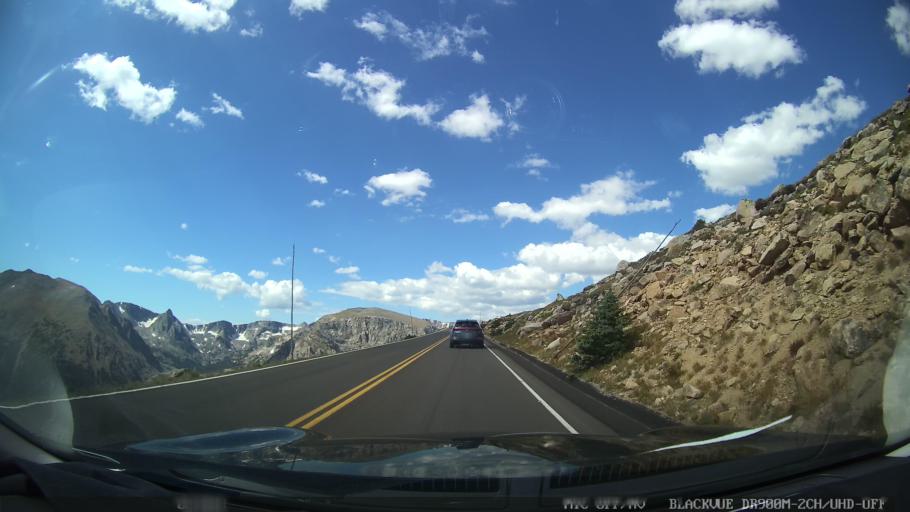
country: US
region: Colorado
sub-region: Larimer County
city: Estes Park
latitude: 40.3943
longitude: -105.7043
